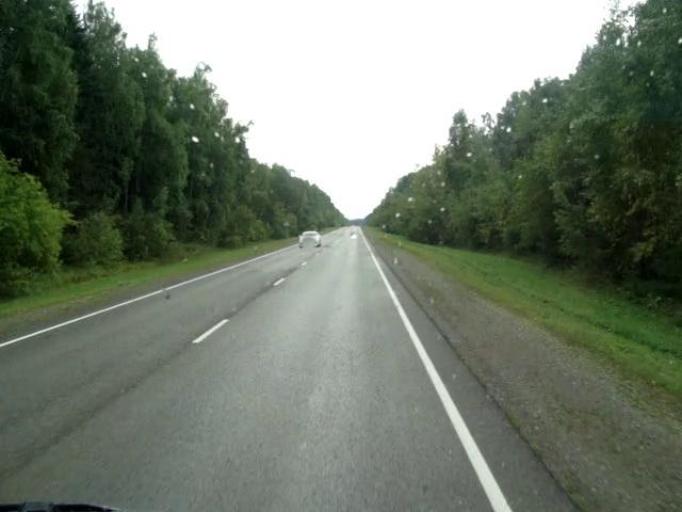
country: RU
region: Altai Krai
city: Shul'gin Log
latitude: 52.1964
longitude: 85.9005
